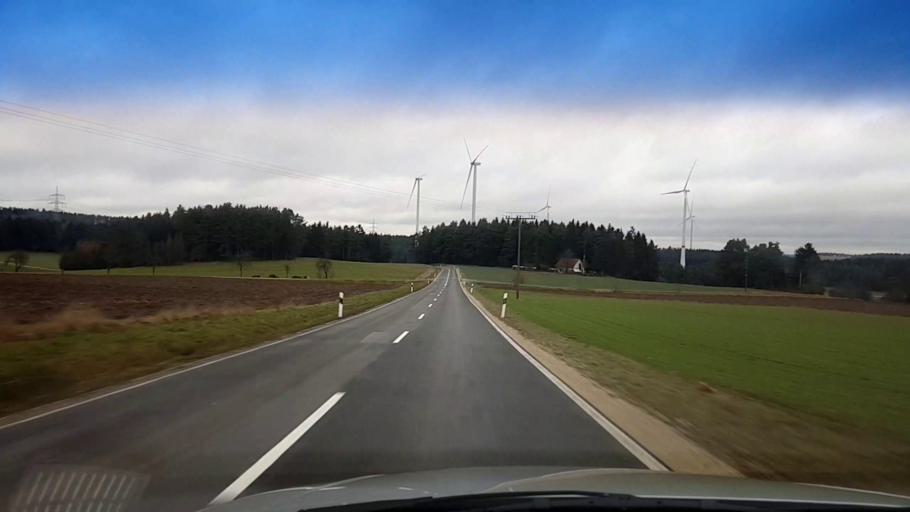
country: DE
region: Bavaria
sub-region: Upper Franconia
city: Wattendorf
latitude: 50.0076
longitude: 11.1336
